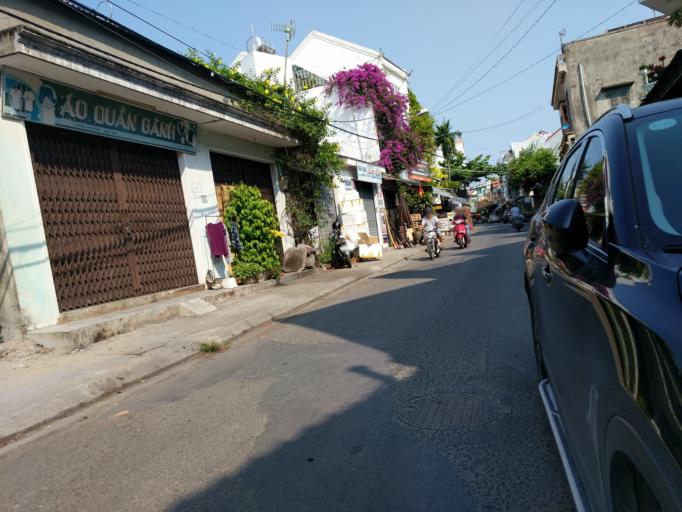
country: VN
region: Quang Nam
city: Hoi An
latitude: 15.8820
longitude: 108.3259
